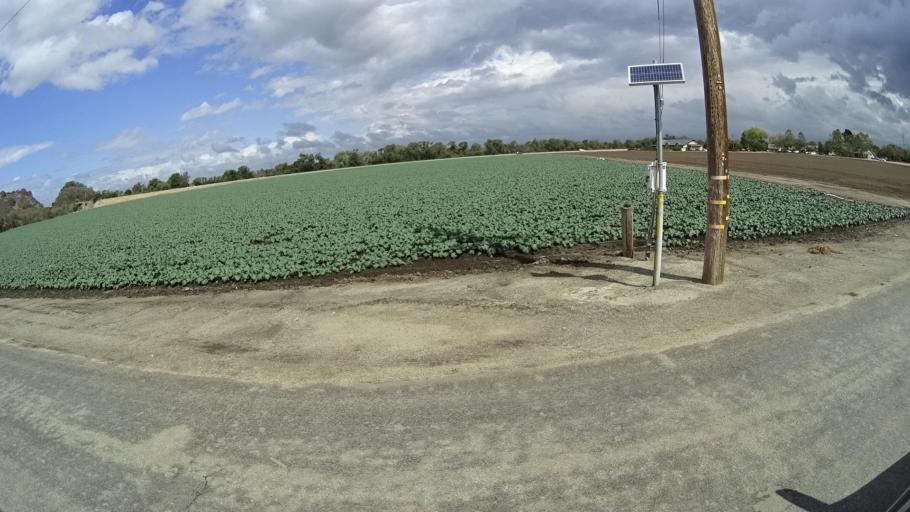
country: US
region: California
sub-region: Monterey County
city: Salinas
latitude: 36.6236
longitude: -121.6864
